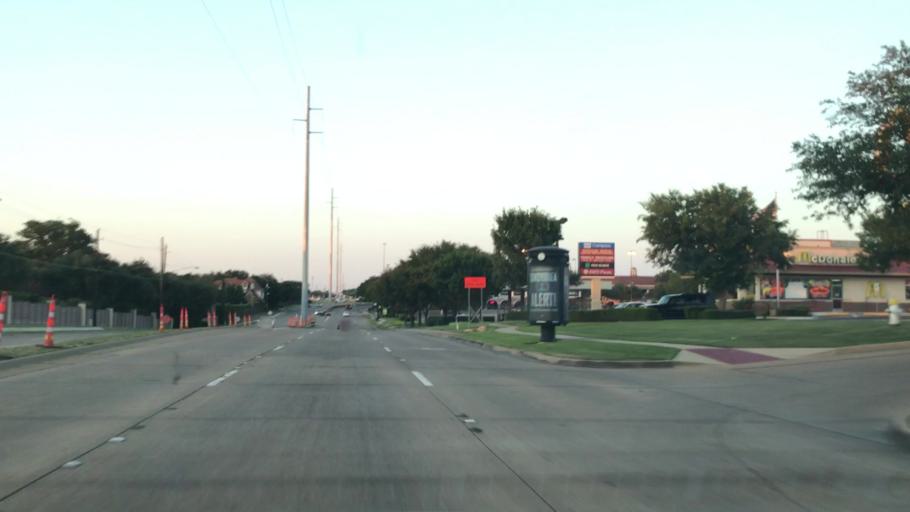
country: US
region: Texas
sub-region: Dallas County
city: Richardson
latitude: 32.8956
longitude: -96.7230
